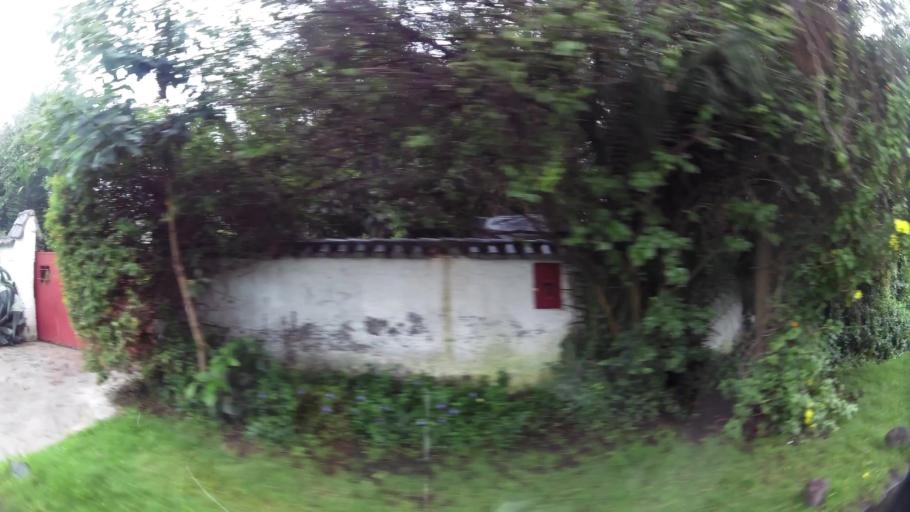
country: EC
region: Pichincha
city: Sangolqui
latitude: -0.2851
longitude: -78.4546
